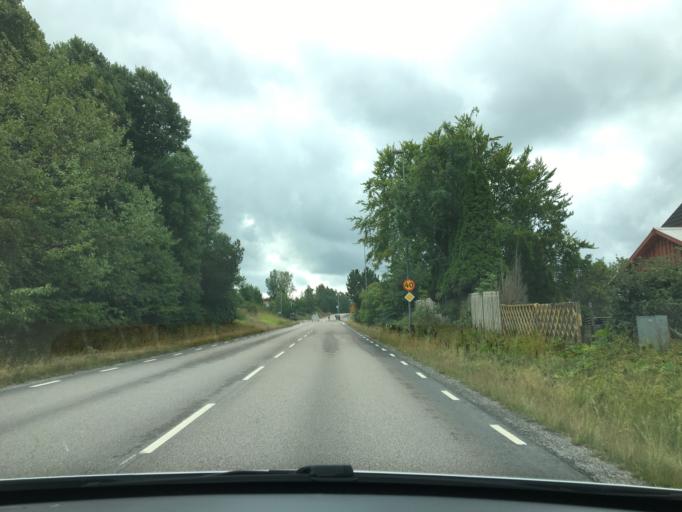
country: SE
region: Vaestra Goetaland
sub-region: Ale Kommun
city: Alvangen
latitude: 57.9547
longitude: 12.1282
